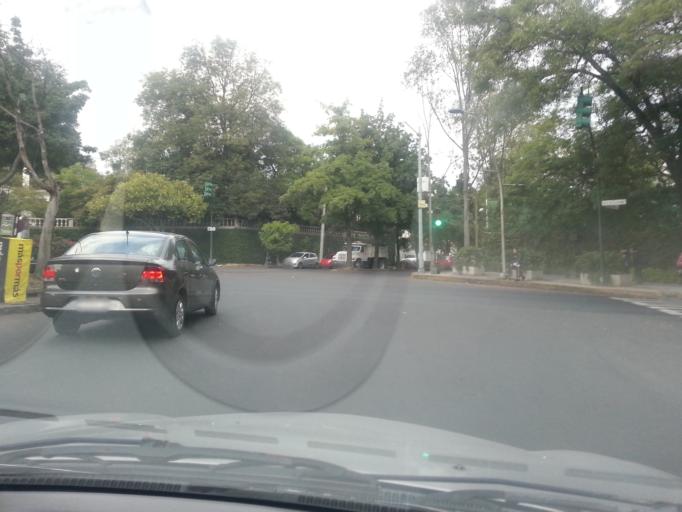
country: MX
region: Mexico City
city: Polanco
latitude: 19.4157
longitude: -99.2188
